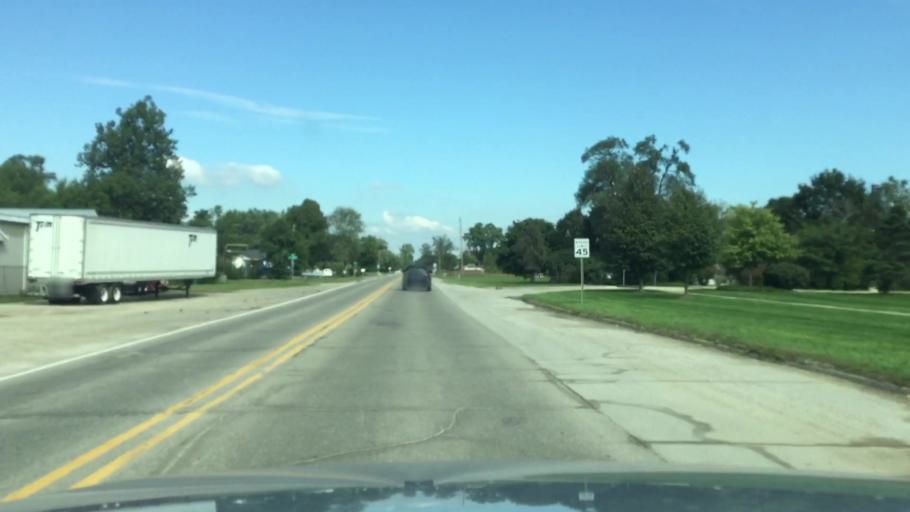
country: US
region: Michigan
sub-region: Wayne County
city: Belleville
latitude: 42.1903
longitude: -83.4834
